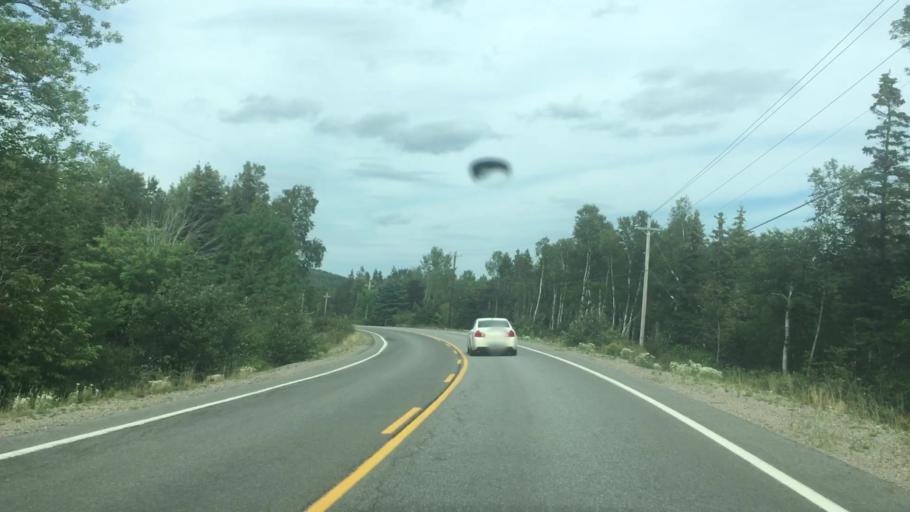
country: CA
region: Nova Scotia
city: Sydney Mines
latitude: 46.5083
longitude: -60.4317
